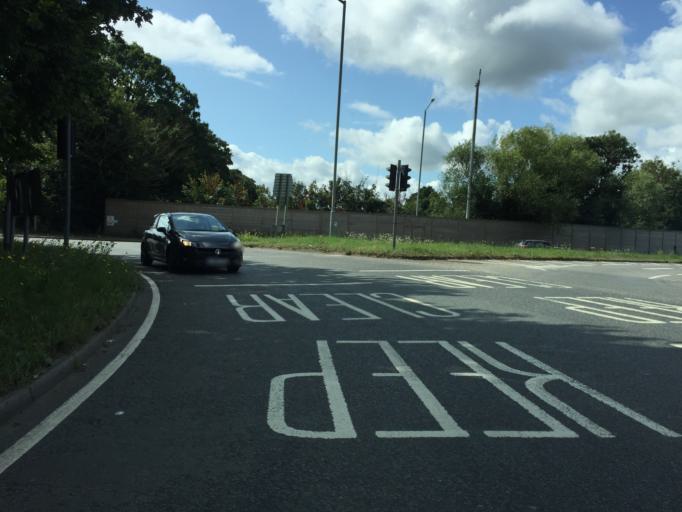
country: GB
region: England
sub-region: Kent
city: Aylesford
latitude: 51.2926
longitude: 0.4832
